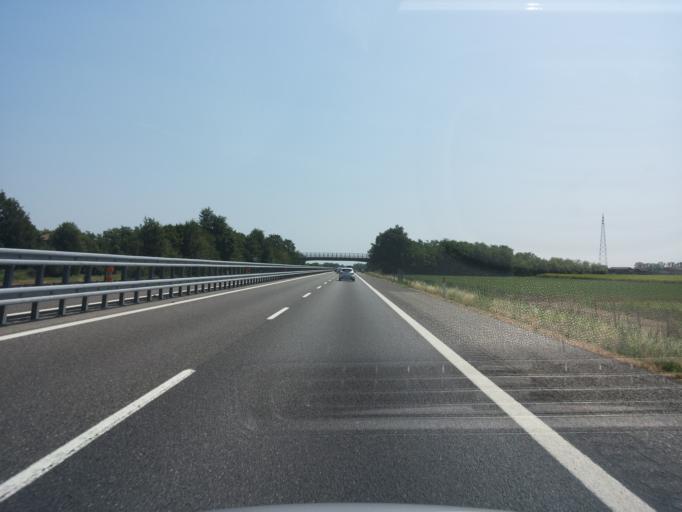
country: IT
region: Emilia-Romagna
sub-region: Provincia di Piacenza
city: Sarmato
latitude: 45.0723
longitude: 9.4776
